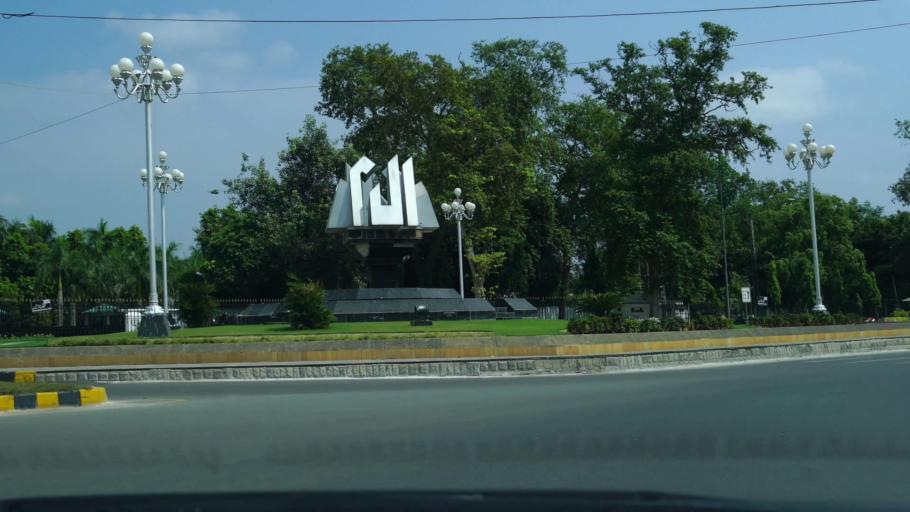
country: PK
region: Punjab
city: Lahore
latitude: 31.5259
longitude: 74.3809
